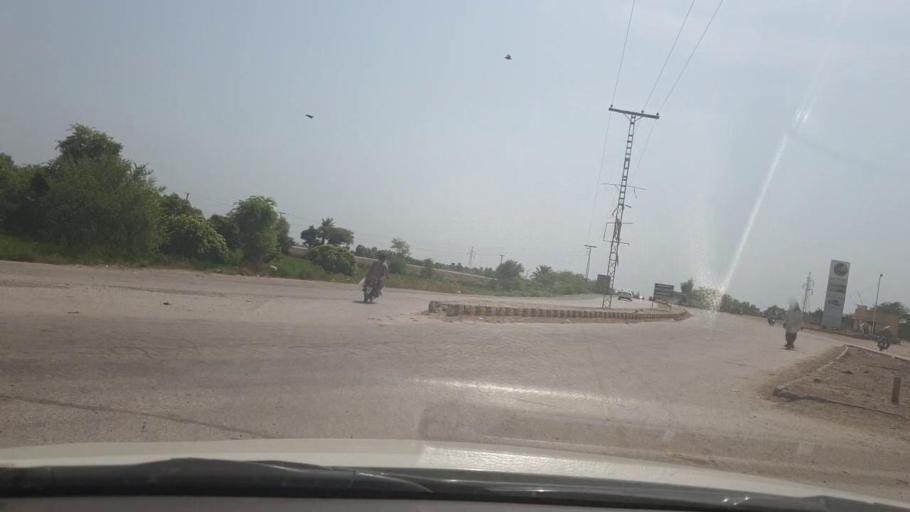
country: PK
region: Sindh
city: Garhi Yasin
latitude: 27.9017
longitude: 68.5051
